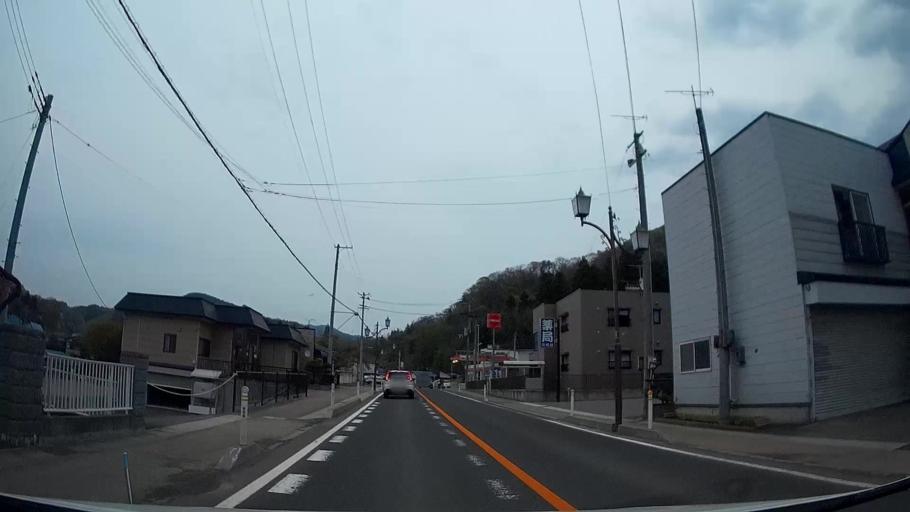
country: JP
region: Akita
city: Hanawa
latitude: 40.2969
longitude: 140.8362
